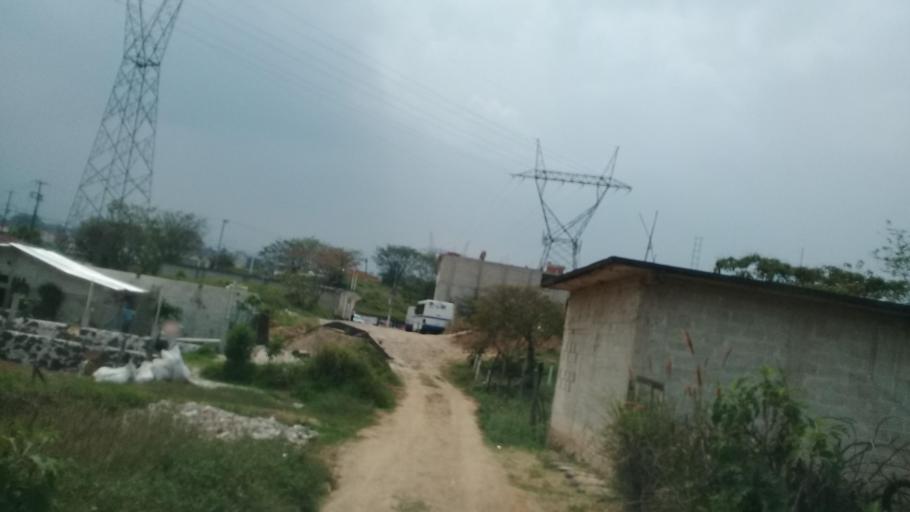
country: MX
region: Veracruz
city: El Castillo
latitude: 19.5601
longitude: -96.8859
